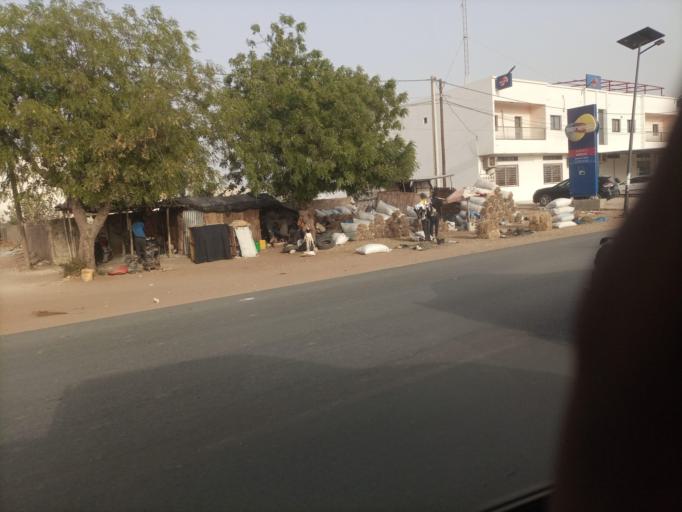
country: SN
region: Thies
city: Warang
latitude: 14.4401
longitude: -16.9786
